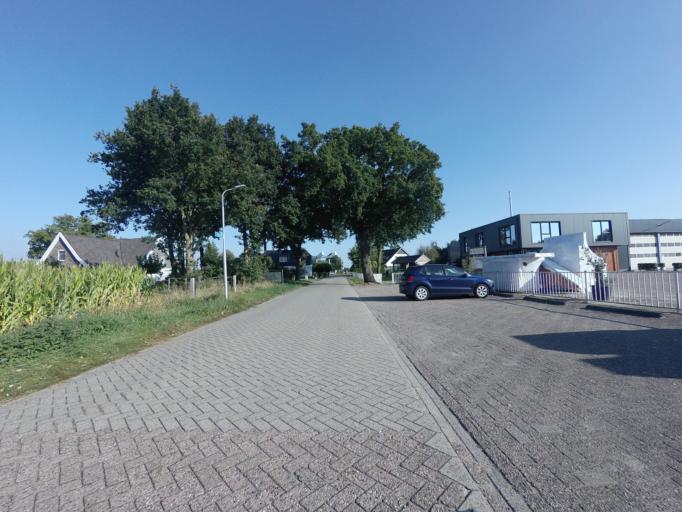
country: NL
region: Overijssel
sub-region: Gemeente Hardenberg
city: Hardenberg
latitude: 52.5602
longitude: 6.6393
